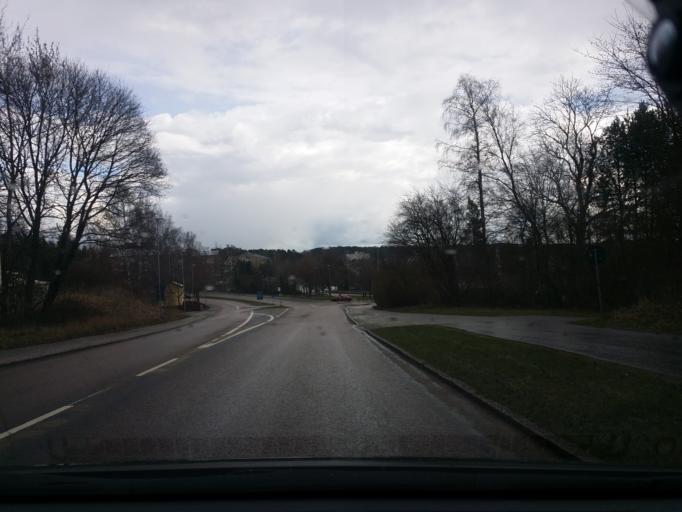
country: SE
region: Uppsala
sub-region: Enkopings Kommun
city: Enkoping
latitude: 59.6426
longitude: 17.0929
